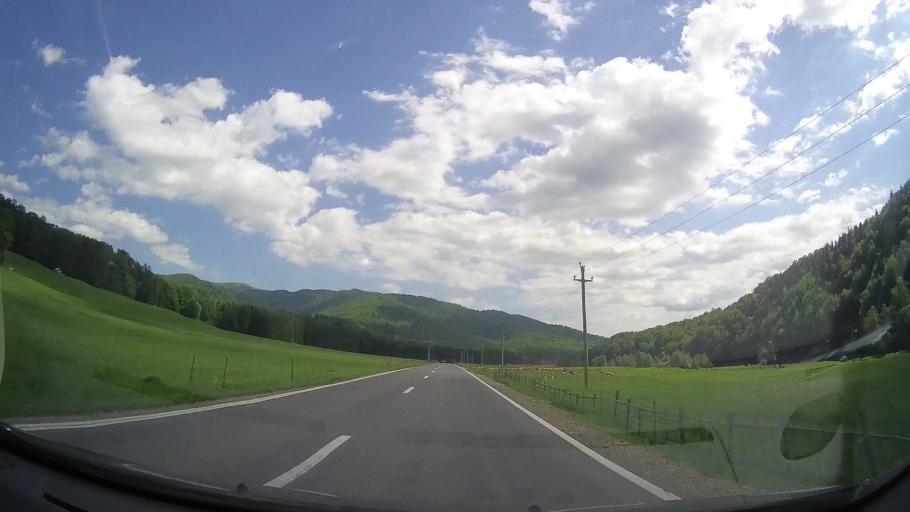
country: RO
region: Prahova
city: Maneciu
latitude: 45.4238
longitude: 25.9416
